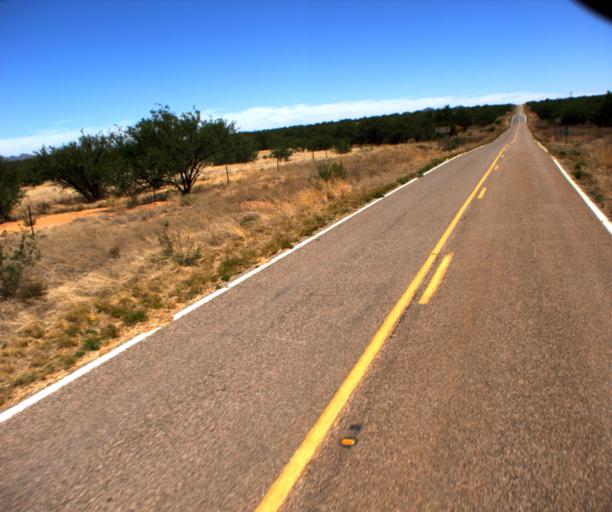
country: US
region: Arizona
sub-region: Santa Cruz County
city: Tubac
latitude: 31.5387
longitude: -111.5406
